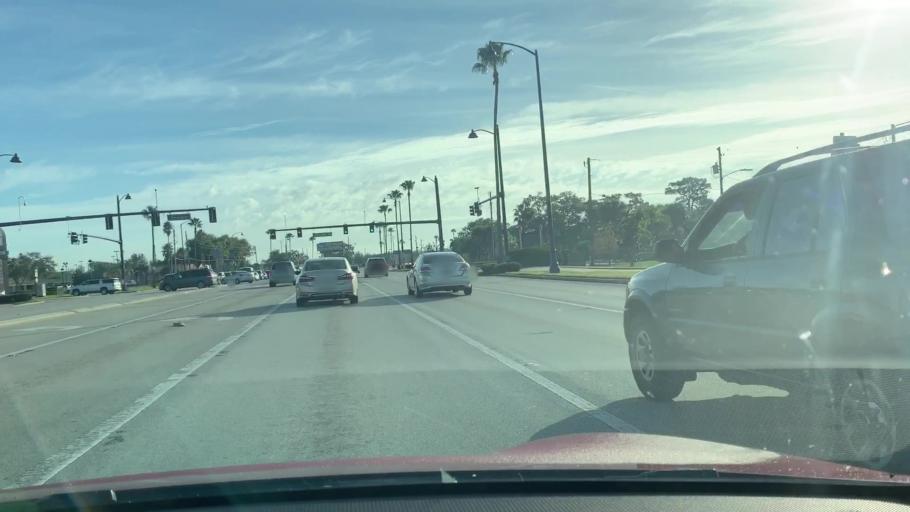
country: US
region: Florida
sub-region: Osceola County
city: Celebration
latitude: 28.3329
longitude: -81.4804
